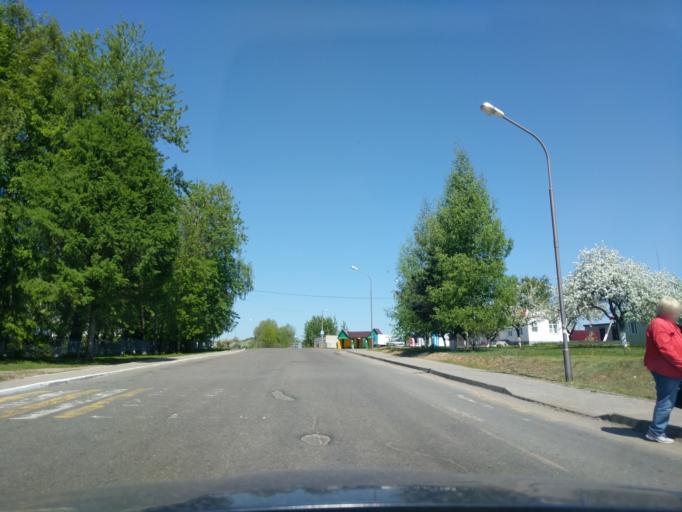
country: BY
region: Minsk
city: Myadzyel
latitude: 54.8875
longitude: 26.9155
